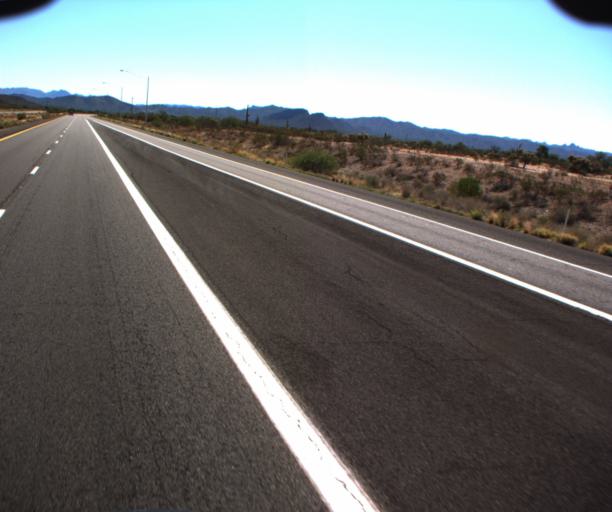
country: US
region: Arizona
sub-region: Pinal County
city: Gold Camp
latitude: 33.2557
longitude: -111.3303
